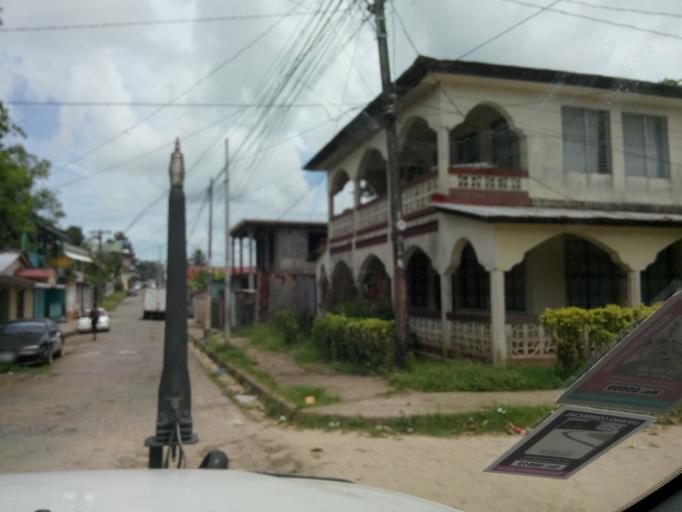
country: NI
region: Atlantico Sur
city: Bluefields
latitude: 12.0076
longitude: -83.7594
